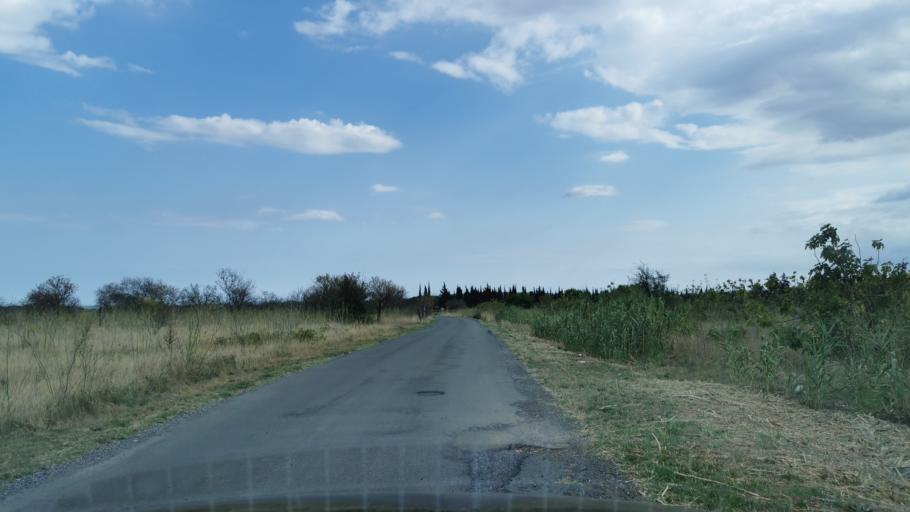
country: FR
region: Languedoc-Roussillon
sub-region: Departement de l'Aude
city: Saint-Marcel-sur-Aude
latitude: 43.2616
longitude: 2.9134
